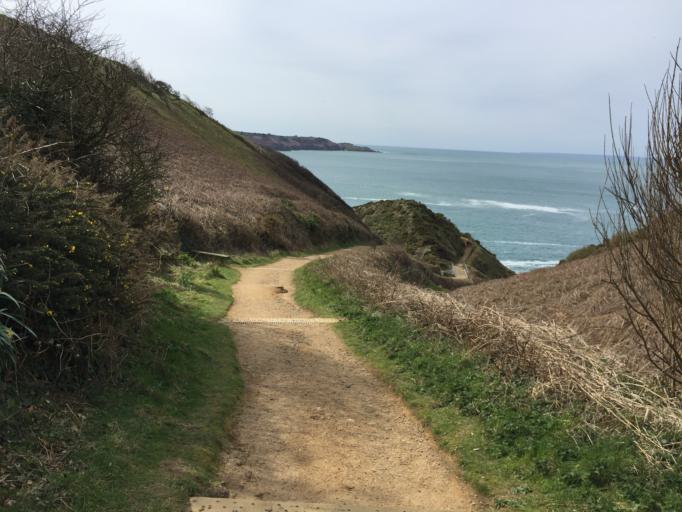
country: JE
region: St Helier
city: Saint Helier
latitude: 49.2515
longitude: -2.1714
